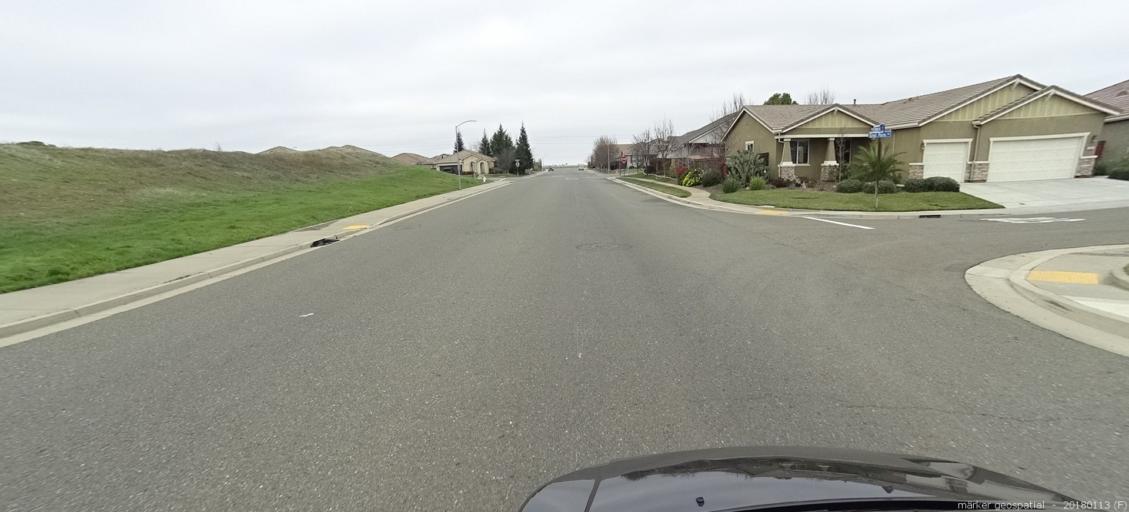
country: US
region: California
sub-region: Sacramento County
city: Gold River
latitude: 38.5564
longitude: -121.2173
